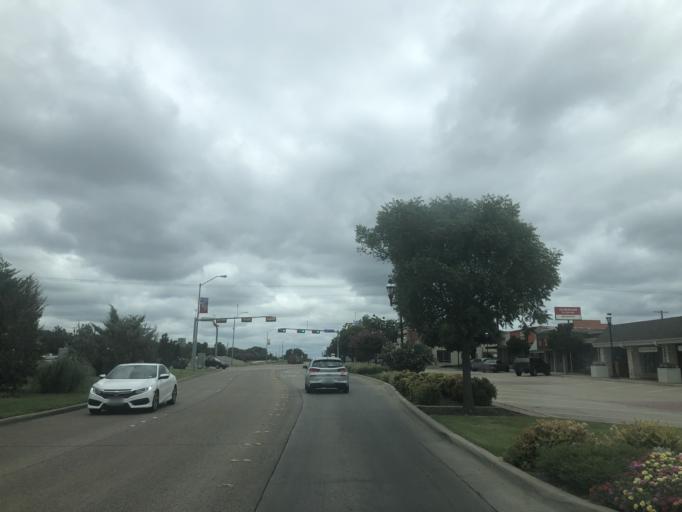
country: US
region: Texas
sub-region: Dallas County
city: Duncanville
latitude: 32.6538
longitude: -96.9082
